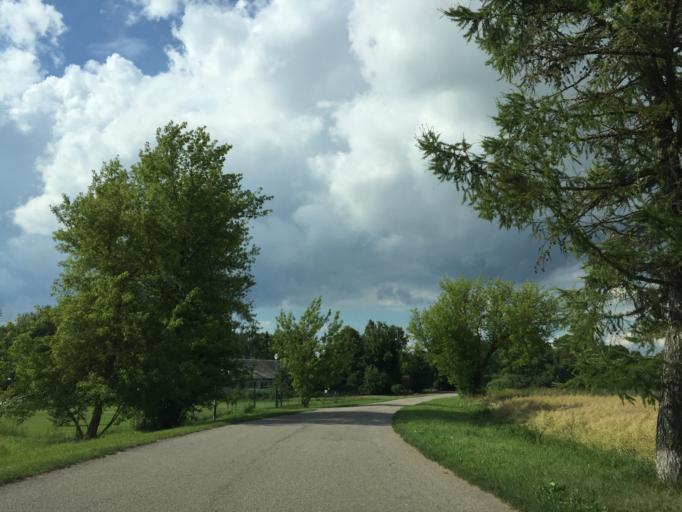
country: LV
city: Tervete
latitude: 56.6092
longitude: 23.4523
